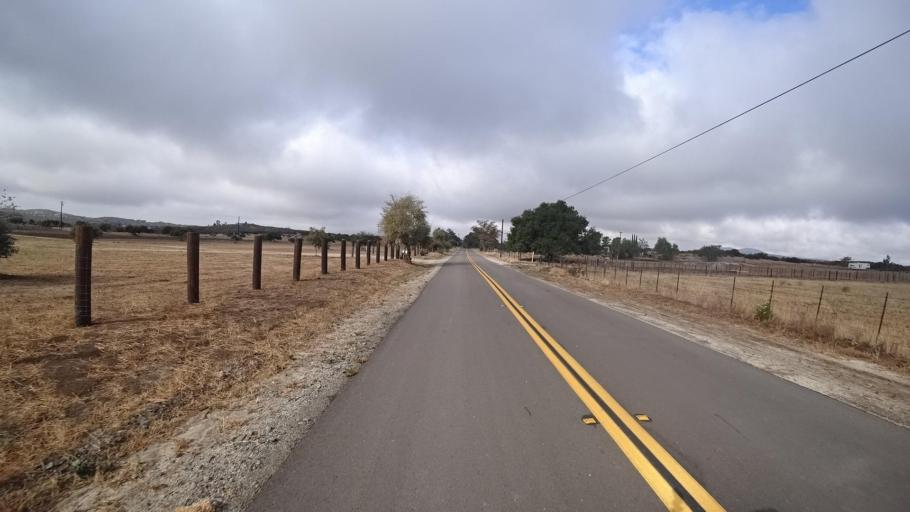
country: MX
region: Baja California
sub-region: Tecate
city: Hacienda Tecate
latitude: 32.6109
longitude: -116.5718
